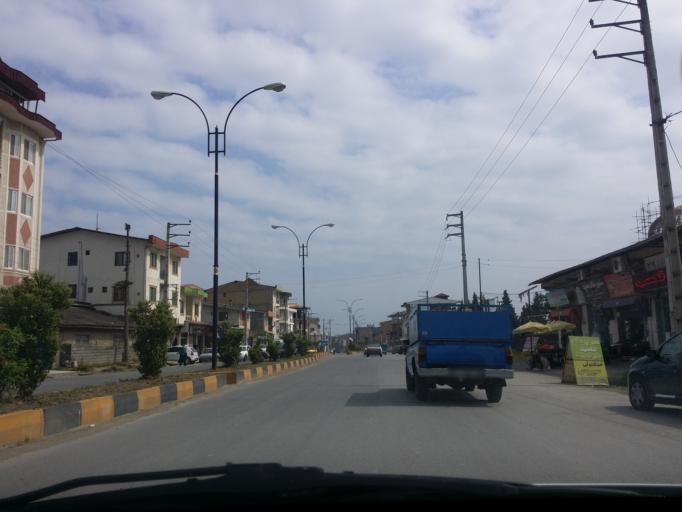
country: IR
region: Mazandaran
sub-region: Nowshahr
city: Nowshahr
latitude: 36.6298
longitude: 51.4851
